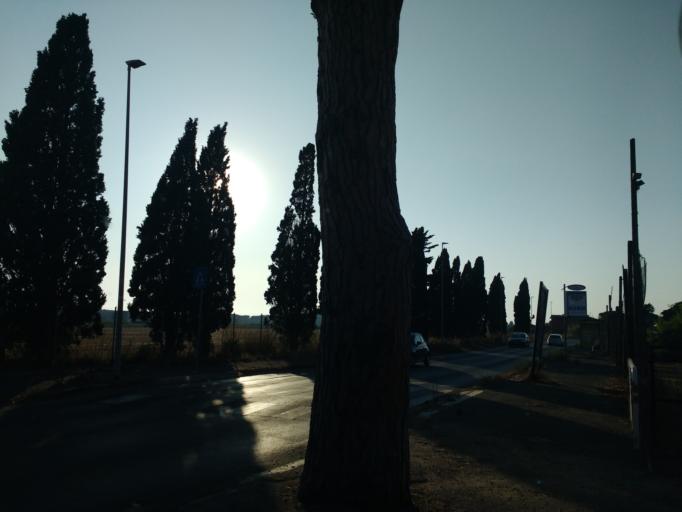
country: IT
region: Latium
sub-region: Citta metropolitana di Roma Capitale
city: Focene
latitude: 41.8343
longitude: 12.2314
